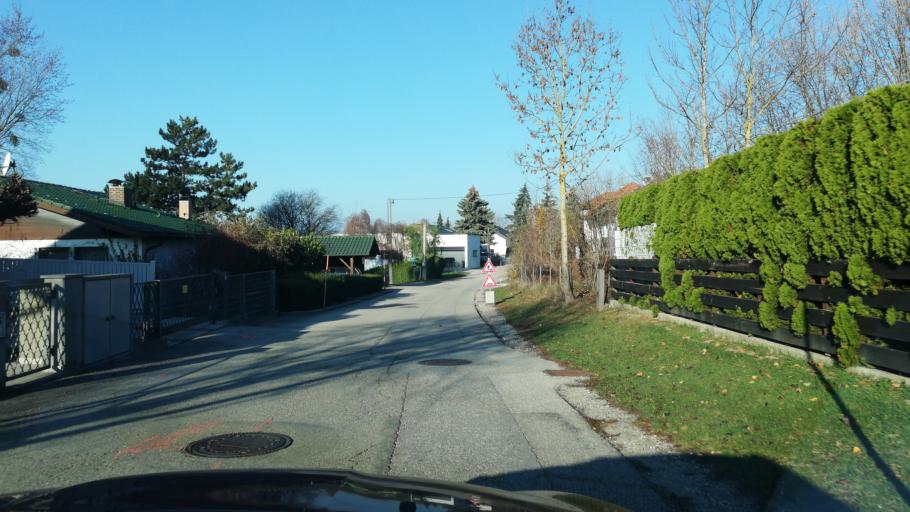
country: AT
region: Upper Austria
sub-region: Wels-Land
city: Buchkirchen
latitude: 48.2490
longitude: 14.0223
